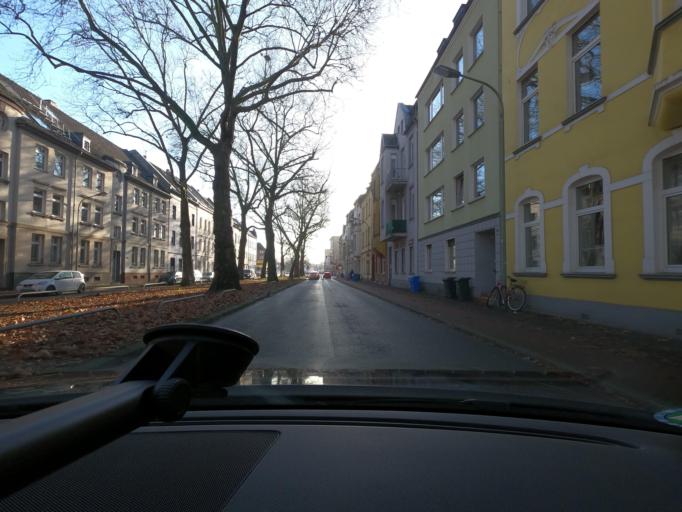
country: DE
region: North Rhine-Westphalia
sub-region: Regierungsbezirk Dusseldorf
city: Krefeld
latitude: 51.3321
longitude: 6.5450
